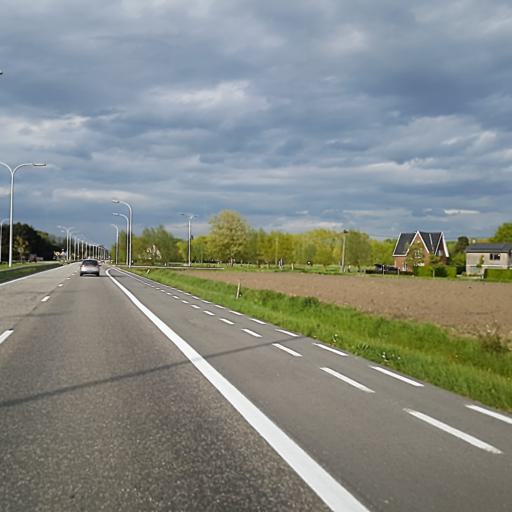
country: BE
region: Flanders
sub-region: Provincie Oost-Vlaanderen
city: De Pinte
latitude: 50.9913
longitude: 3.6799
